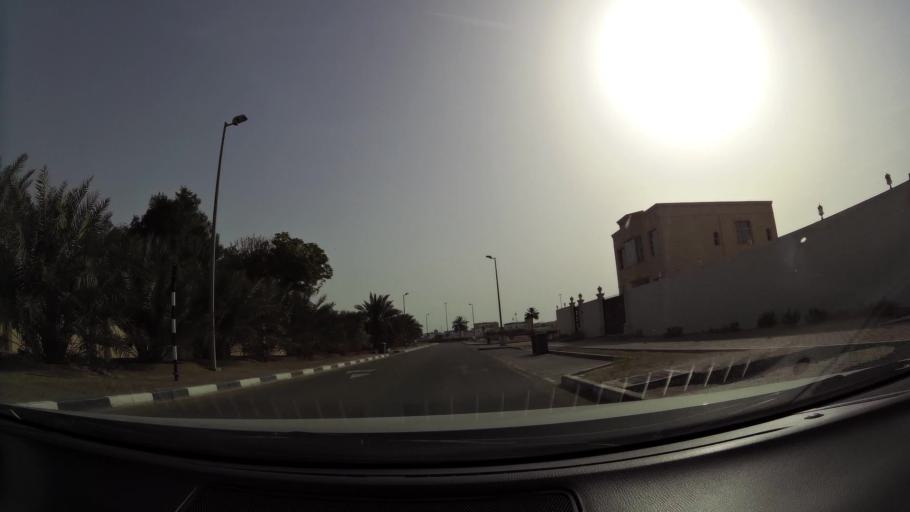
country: AE
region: Abu Dhabi
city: Al Ain
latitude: 24.1323
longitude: 55.7010
